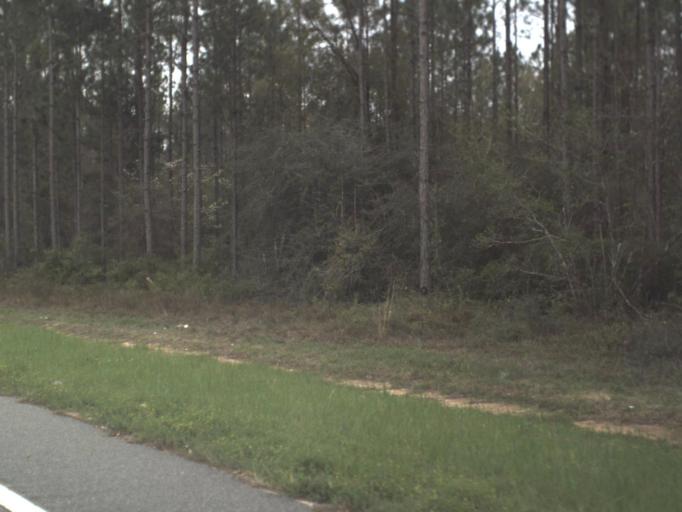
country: US
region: Florida
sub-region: Gulf County
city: Wewahitchka
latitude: 30.2415
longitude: -85.2186
